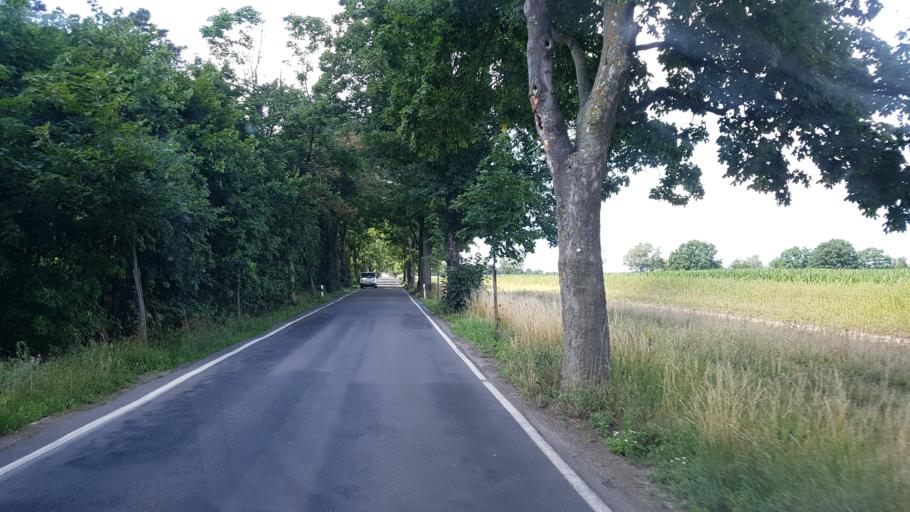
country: DE
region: Brandenburg
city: Senftenberg
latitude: 51.4894
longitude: 14.0815
